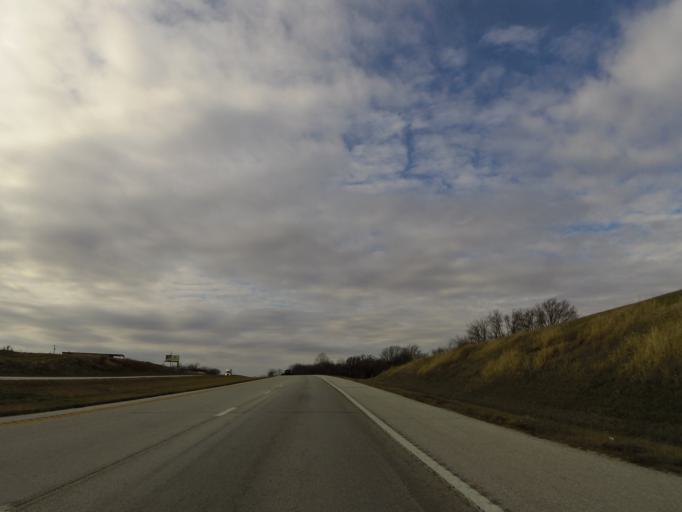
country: US
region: Missouri
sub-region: Marion County
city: Hannibal
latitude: 39.7412
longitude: -91.4193
